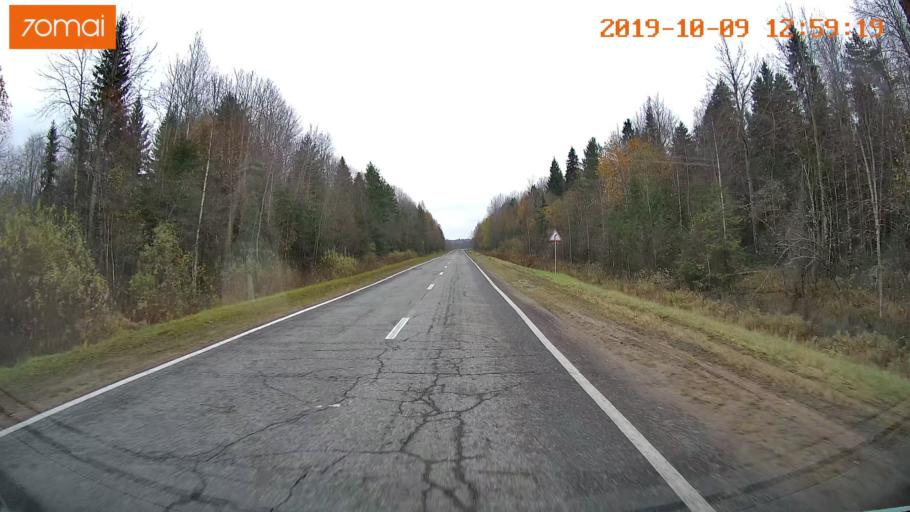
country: RU
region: Jaroslavl
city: Prechistoye
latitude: 58.3840
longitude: 40.4620
